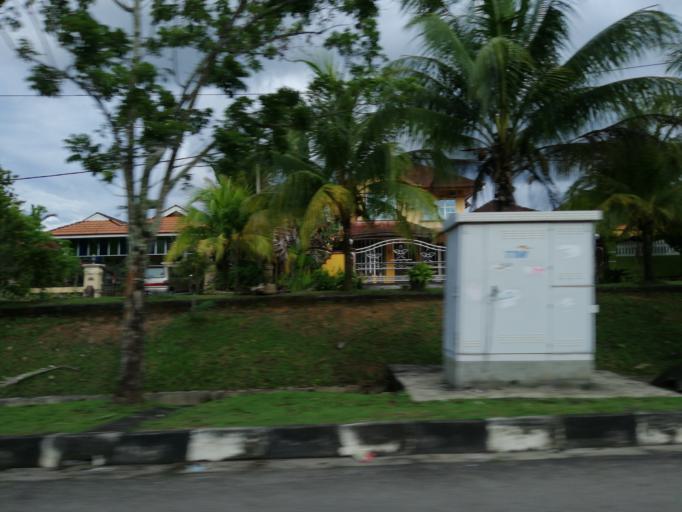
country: MY
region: Penang
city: Tasek Glugor
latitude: 5.5034
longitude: 100.6246
